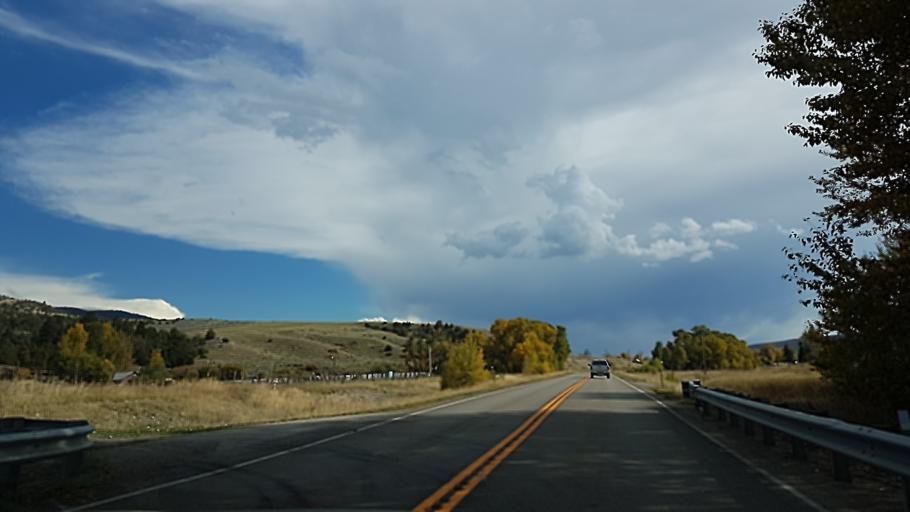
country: US
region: Montana
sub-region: Jefferson County
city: Whitehall
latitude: 45.8056
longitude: -111.9278
